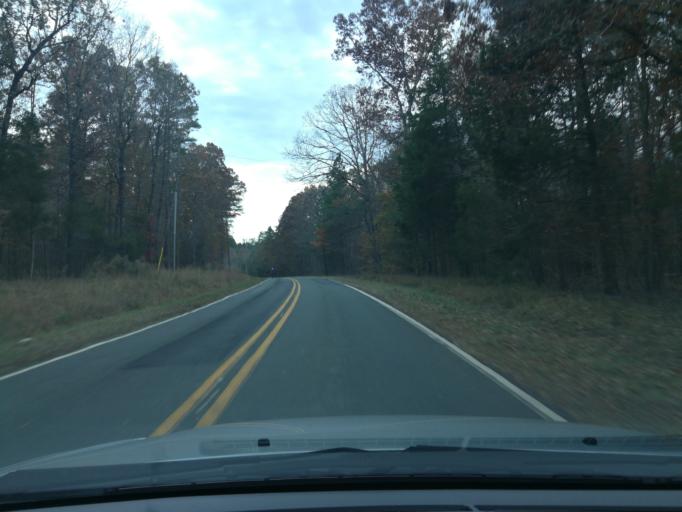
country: US
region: North Carolina
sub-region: Orange County
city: Hillsborough
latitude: 36.0110
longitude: -79.0446
